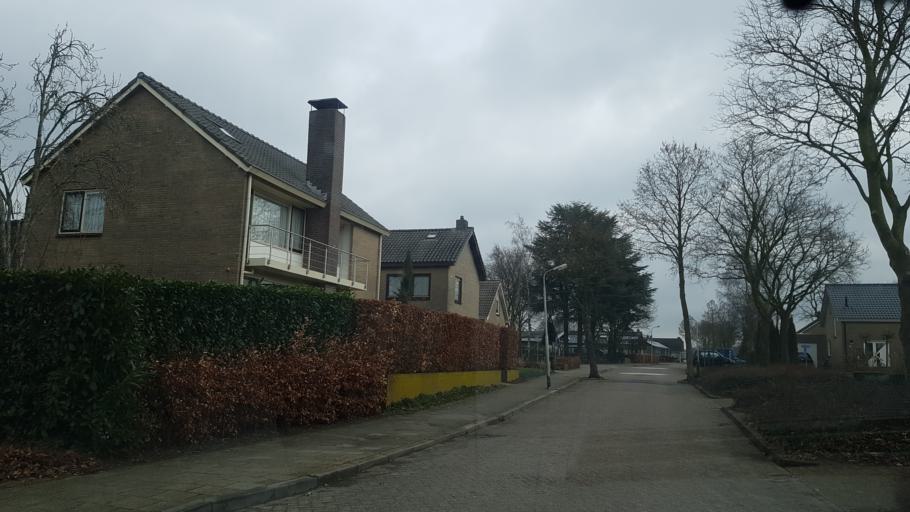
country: NL
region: Drenthe
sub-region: Gemeente Hoogeveen
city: Hoogeveen
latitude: 52.6731
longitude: 6.4333
